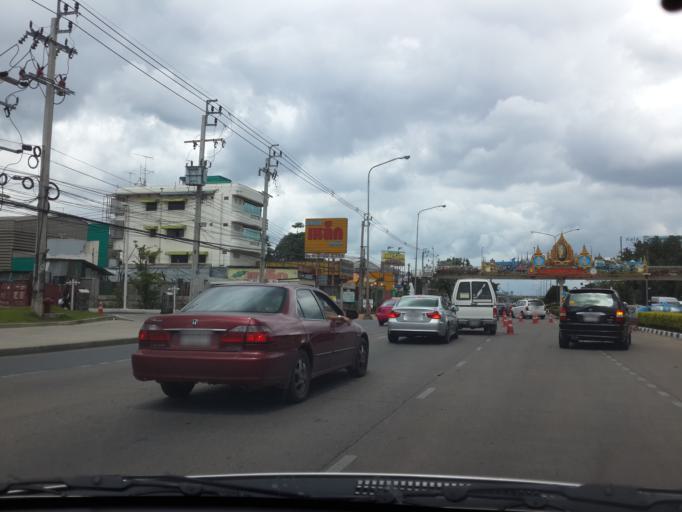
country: TH
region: Bangkok
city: Bueng Kum
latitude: 13.7740
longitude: 100.6681
